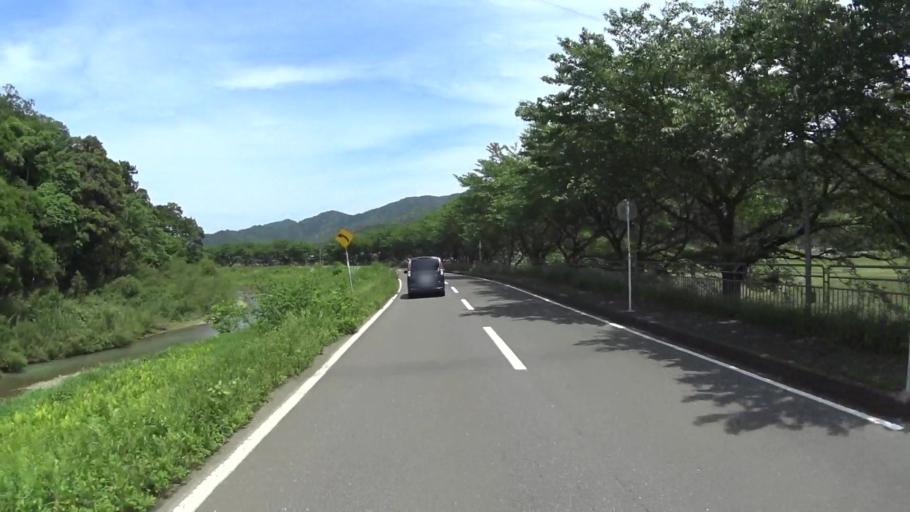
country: JP
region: Fukui
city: Obama
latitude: 35.4576
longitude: 135.6042
